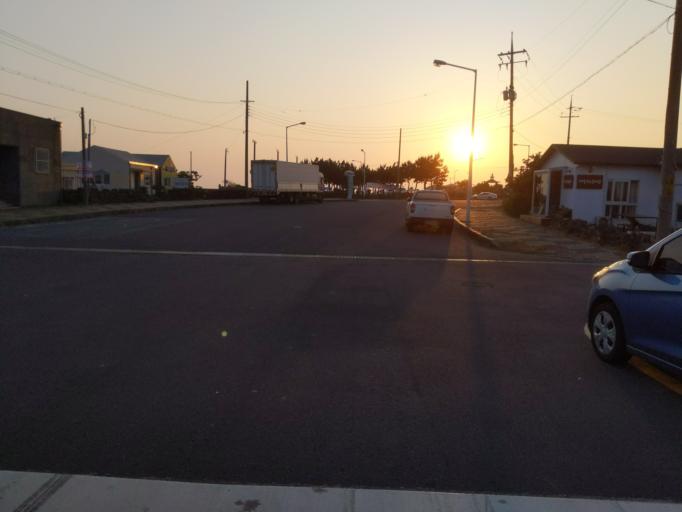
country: KR
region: Jeju-do
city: Gaigeturi
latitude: 33.2208
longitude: 126.2481
